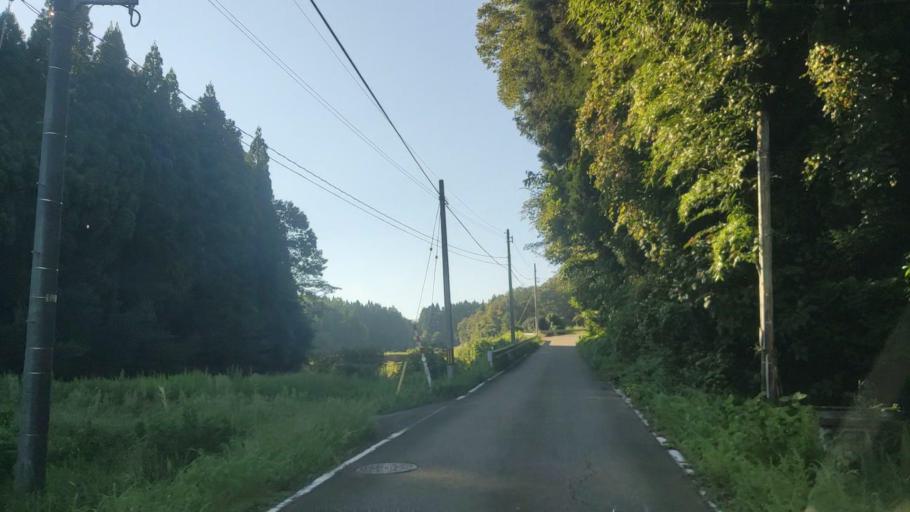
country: JP
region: Ishikawa
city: Nanao
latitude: 37.1285
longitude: 136.8951
